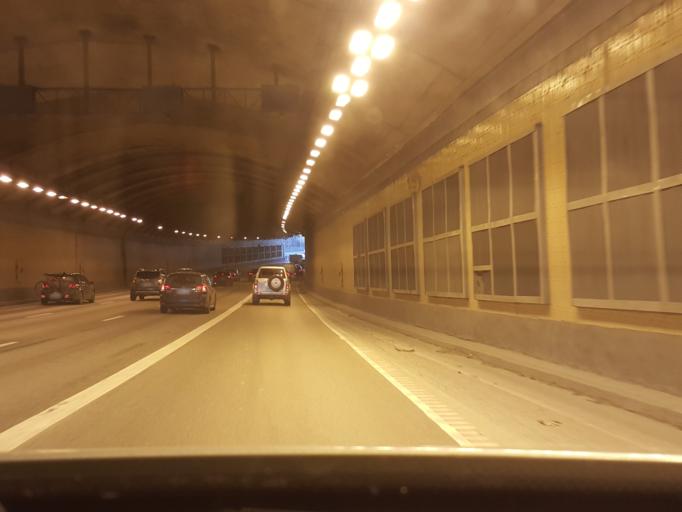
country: SE
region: Stockholm
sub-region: Solna Kommun
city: Solna
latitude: 59.3289
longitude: 18.0088
